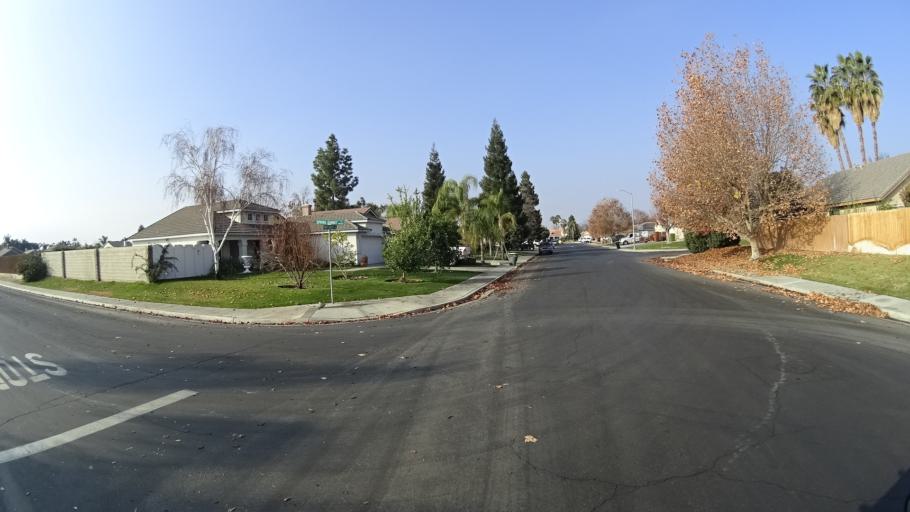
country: US
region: California
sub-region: Kern County
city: Greenfield
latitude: 35.3004
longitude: -119.0675
